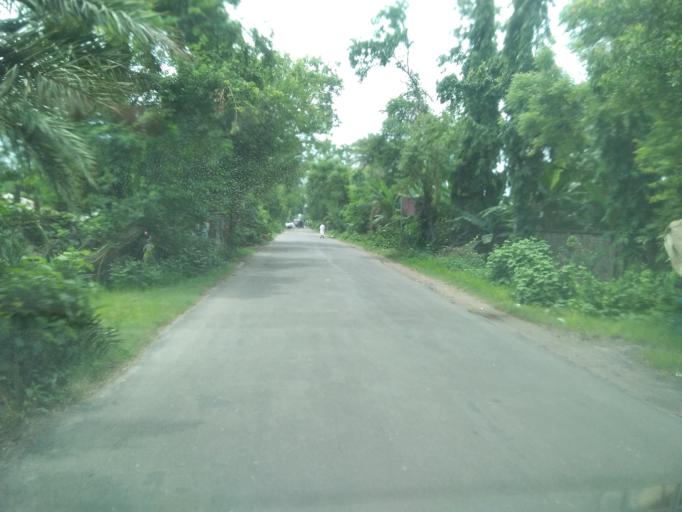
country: IN
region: West Bengal
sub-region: North 24 Parganas
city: Taki
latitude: 22.5764
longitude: 88.9989
